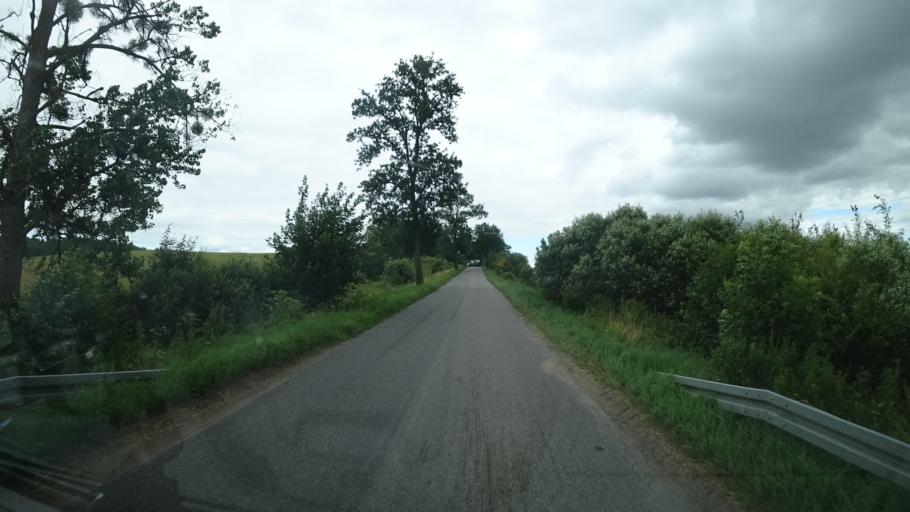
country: PL
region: Podlasie
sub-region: Powiat suwalski
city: Filipow
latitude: 54.2825
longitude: 22.5243
